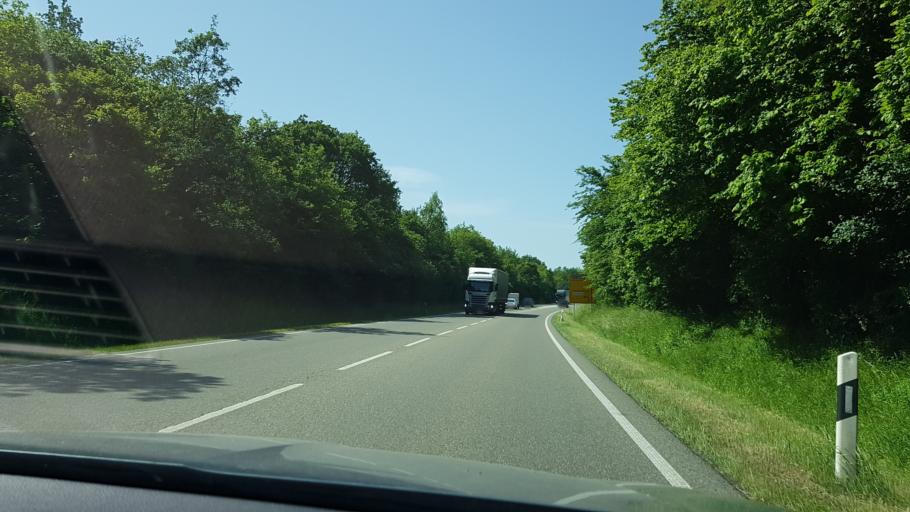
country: DE
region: Bavaria
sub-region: Upper Bavaria
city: Schongeising
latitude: 48.1556
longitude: 11.2160
